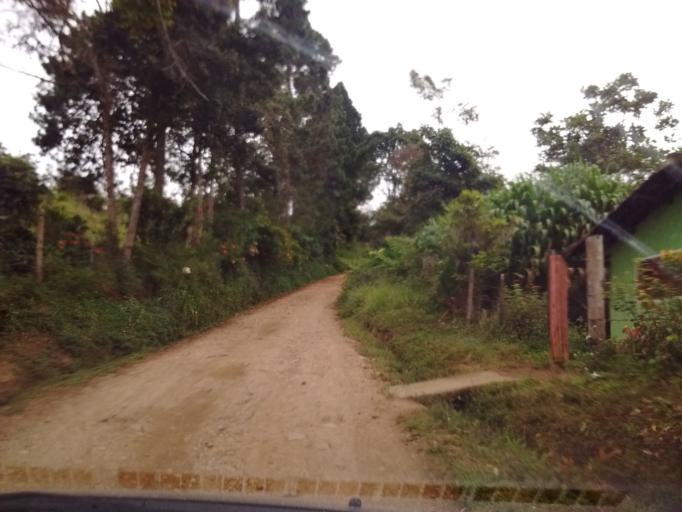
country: CO
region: Huila
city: San Agustin
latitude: 1.9057
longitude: -76.3023
